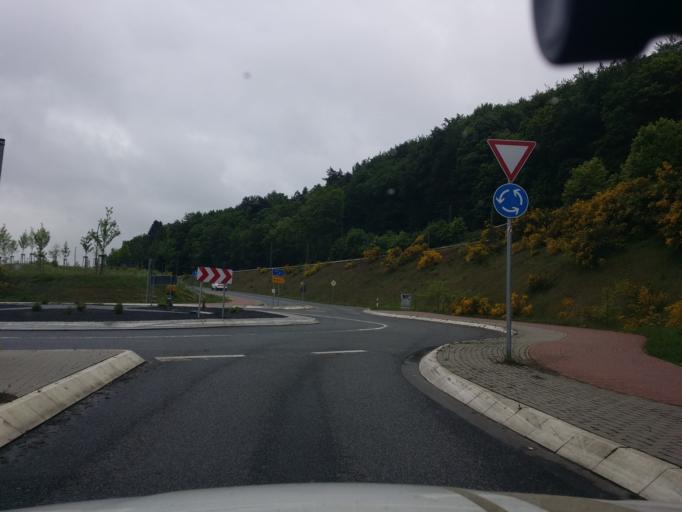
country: DE
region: Hesse
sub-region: Regierungsbezirk Darmstadt
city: Niedernhausen
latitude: 50.1539
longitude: 8.3231
